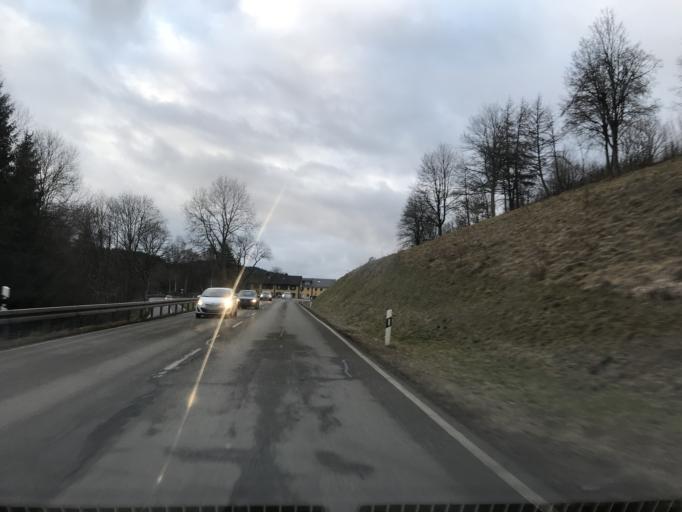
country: DE
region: Baden-Wuerttemberg
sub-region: Freiburg Region
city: Friedenweiler
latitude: 47.9058
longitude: 8.2307
